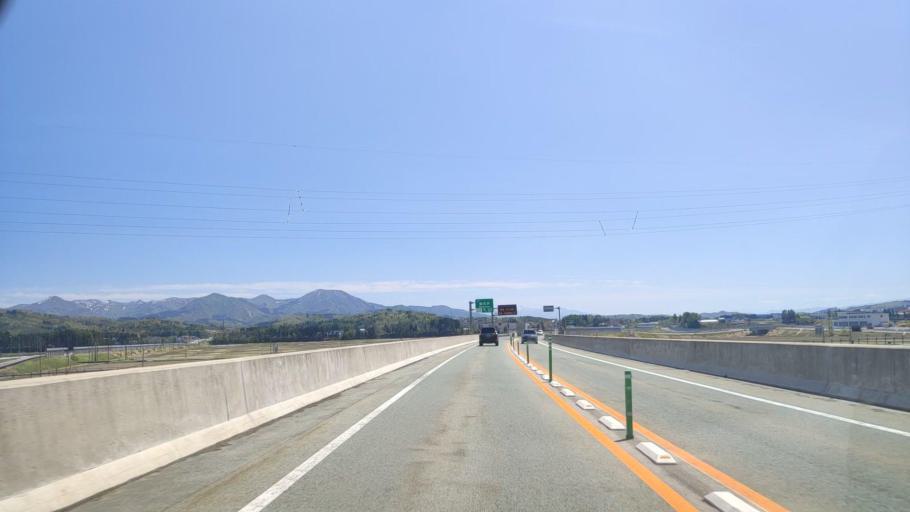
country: JP
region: Yamagata
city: Obanazawa
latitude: 38.6112
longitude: 140.3883
